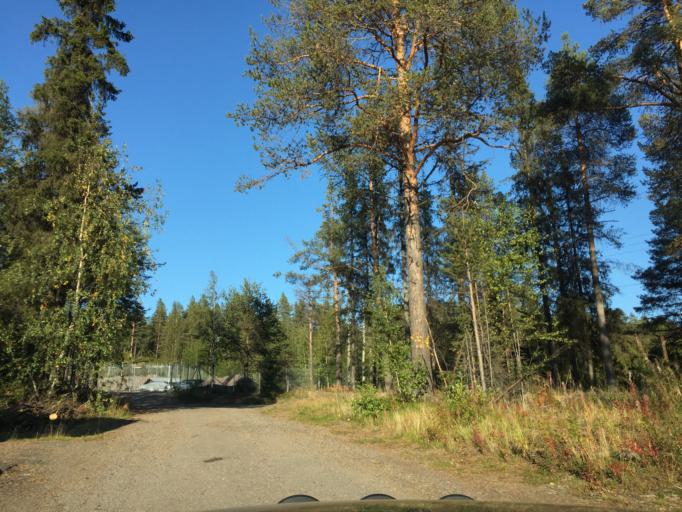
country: SE
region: Norrbotten
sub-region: Gallivare Kommun
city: Malmberget
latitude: 67.6539
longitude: 21.0373
